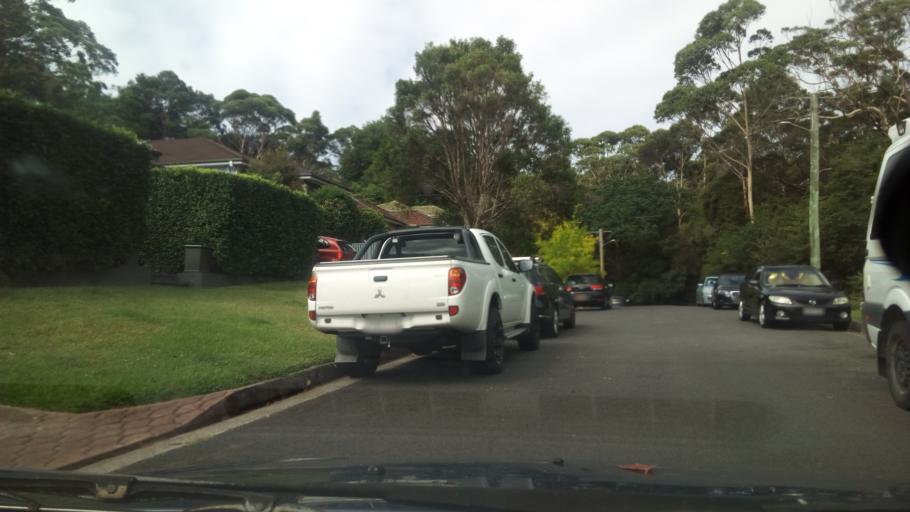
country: AU
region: New South Wales
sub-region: Wollongong
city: Mangerton
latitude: -34.4344
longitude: 150.8728
